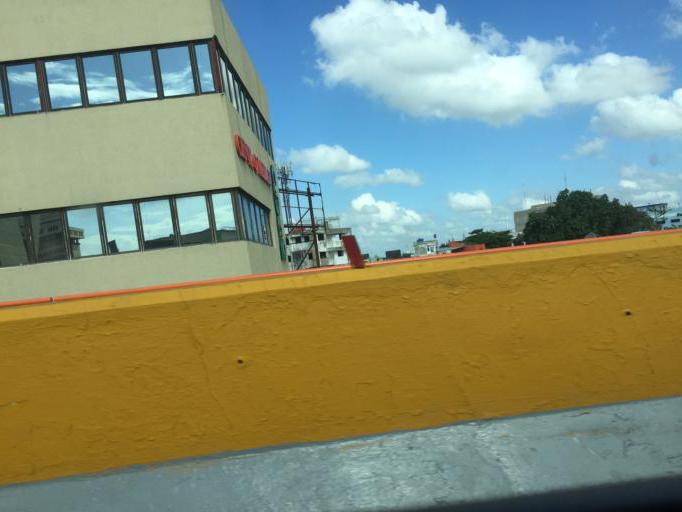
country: DO
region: Nacional
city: San Carlos
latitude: 18.4762
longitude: -69.9056
